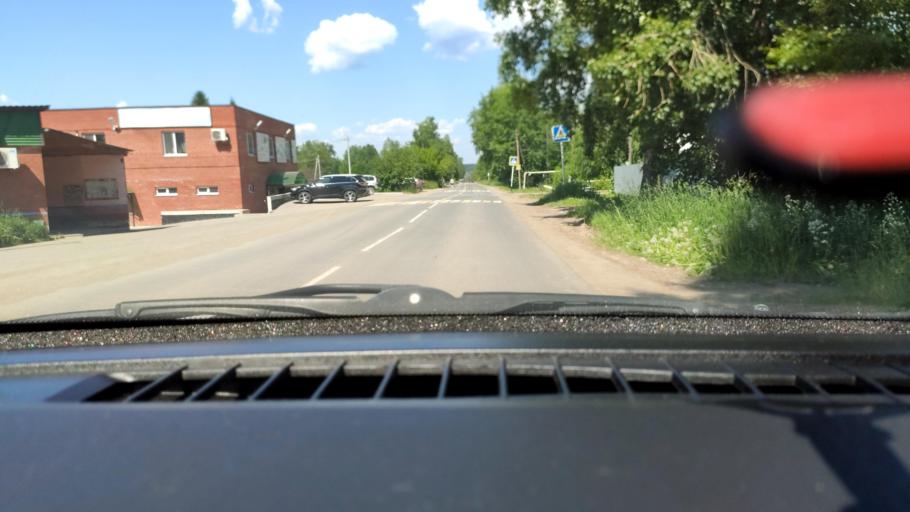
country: RU
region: Perm
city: Sylva
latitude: 58.0320
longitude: 56.7592
